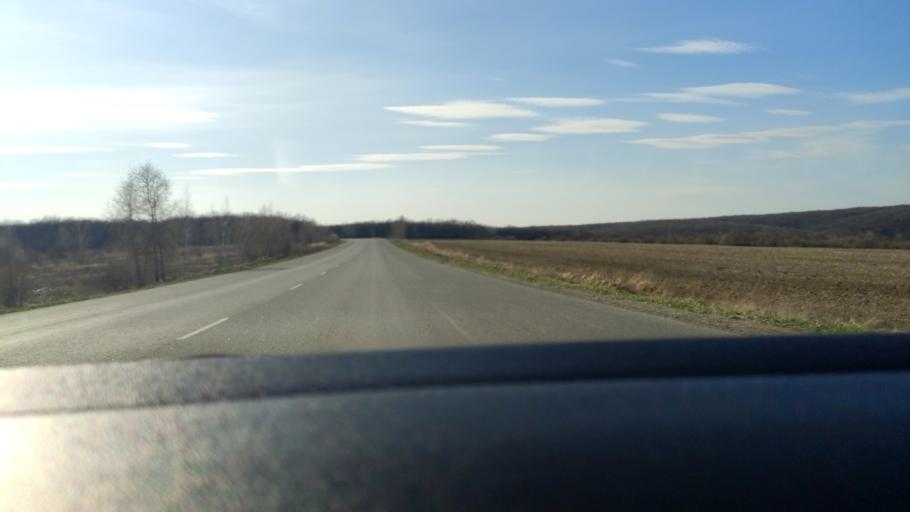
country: RU
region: Voronezj
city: Kolodeznyy
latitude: 51.3384
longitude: 39.0787
